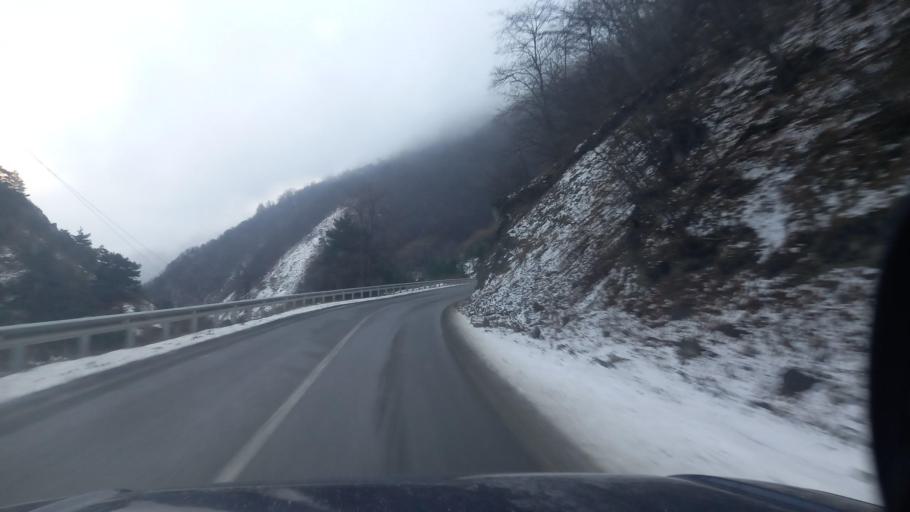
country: RU
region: Ingushetiya
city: Dzhayrakh
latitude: 42.7918
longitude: 44.7673
